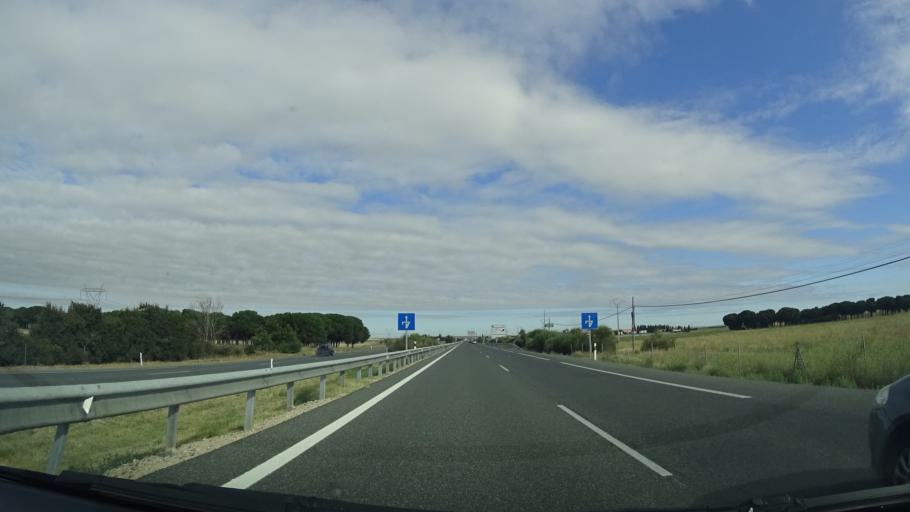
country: ES
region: Castille and Leon
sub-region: Provincia de Valladolid
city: San Vicente del Palacio
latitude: 41.2159
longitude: -4.8379
